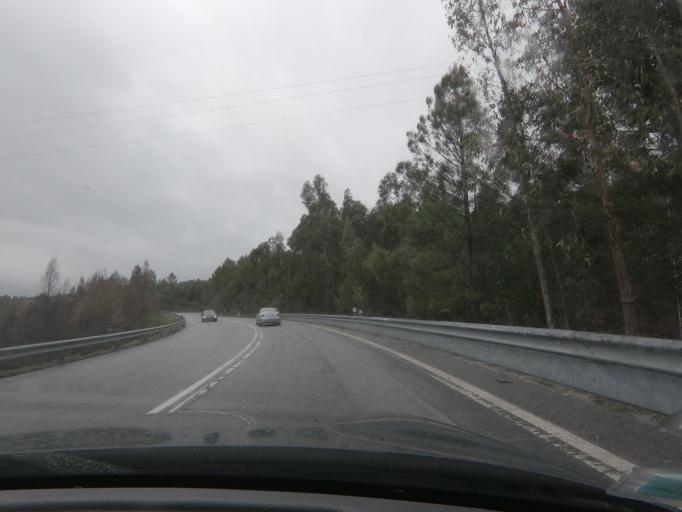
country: PT
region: Braga
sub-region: Celorico de Basto
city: Celorico de Basto
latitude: 41.3490
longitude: -8.0214
